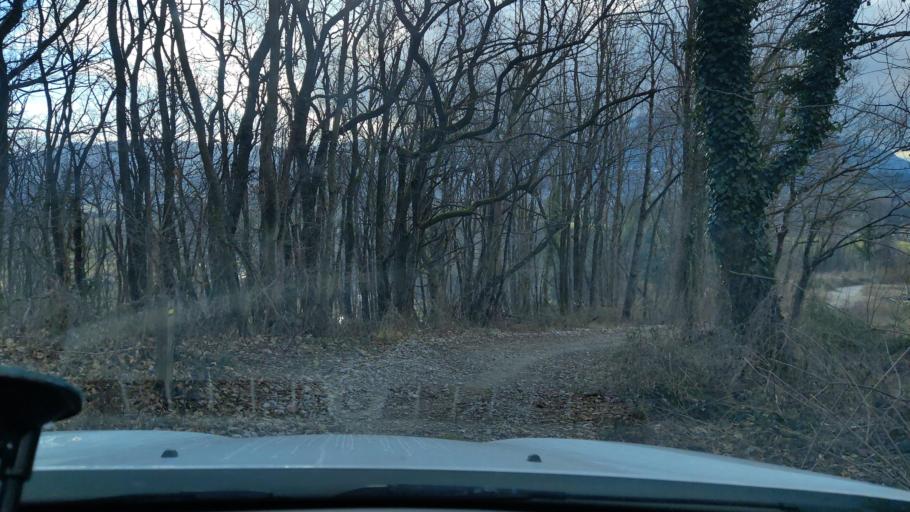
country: FR
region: Rhone-Alpes
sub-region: Departement de la Savoie
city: La Motte-Servolex
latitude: 45.5734
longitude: 5.8734
